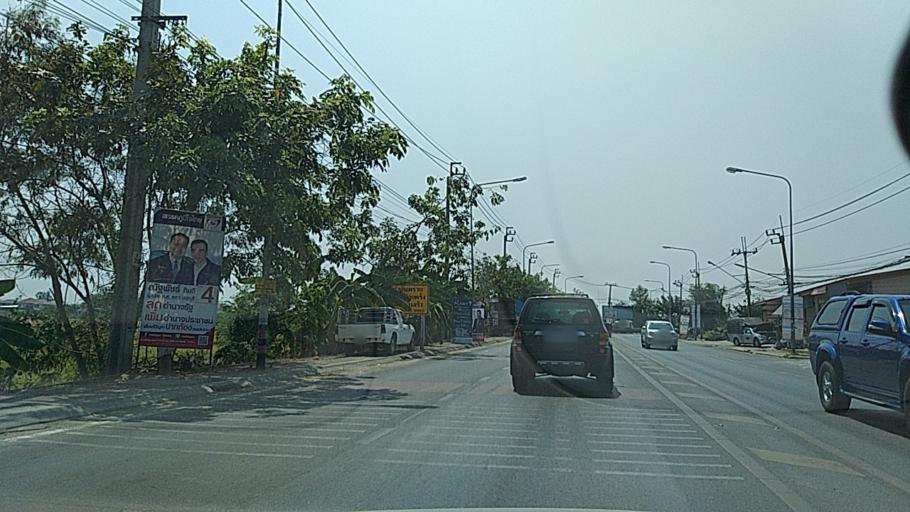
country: TH
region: Nonthaburi
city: Bang Bua Thong
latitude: 13.9084
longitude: 100.3777
